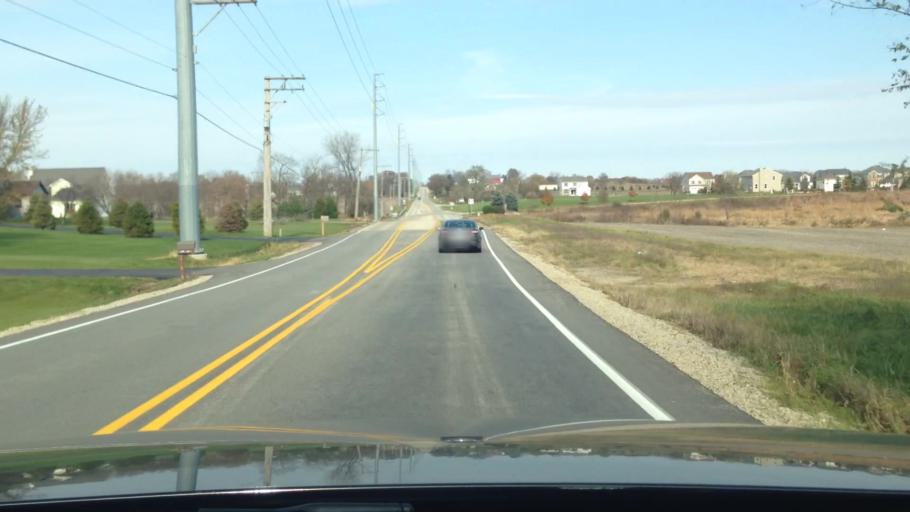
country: US
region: Illinois
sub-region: McHenry County
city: Woodstock
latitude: 42.2799
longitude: -88.4525
